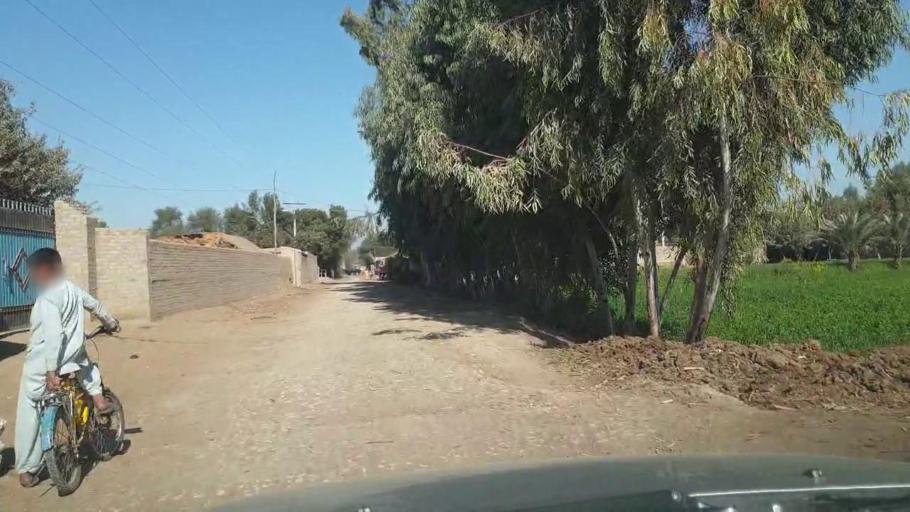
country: PK
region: Sindh
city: Ghotki
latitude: 28.0984
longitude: 69.3423
